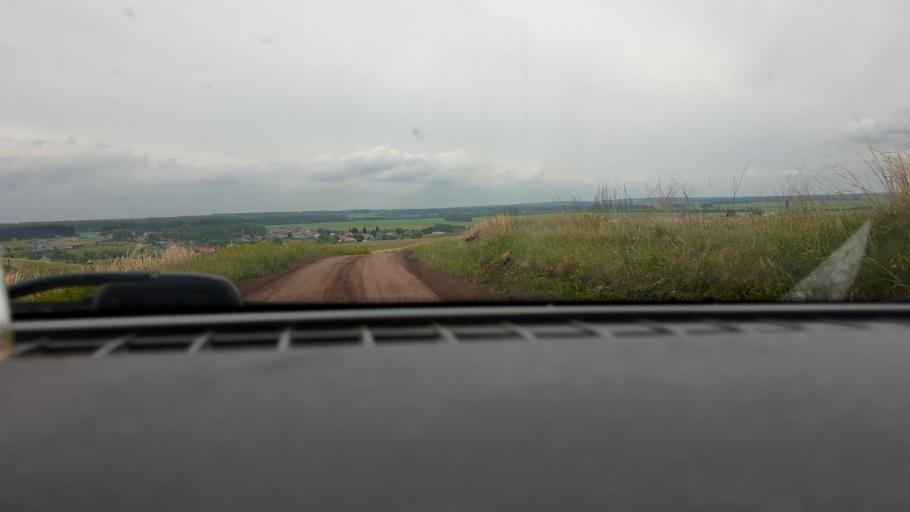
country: RU
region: Bashkortostan
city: Chishmy
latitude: 54.6906
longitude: 55.4854
